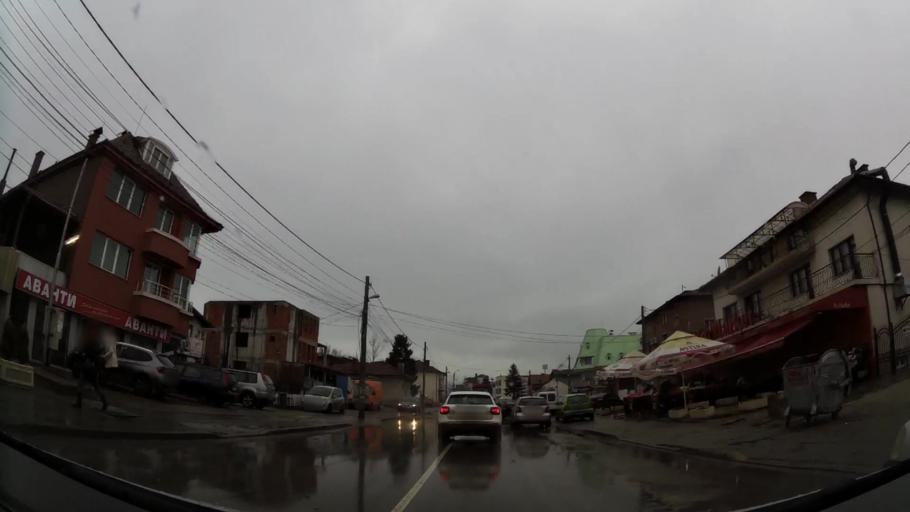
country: BG
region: Sofia-Capital
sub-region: Stolichna Obshtina
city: Sofia
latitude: 42.6278
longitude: 23.4075
